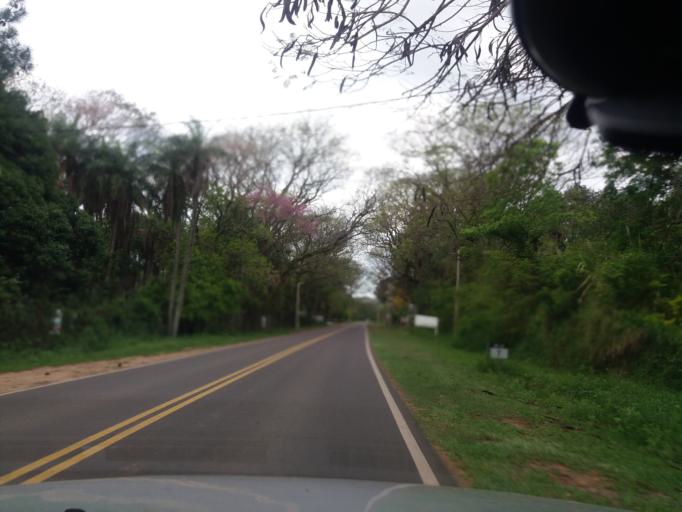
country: AR
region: Corrientes
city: Riachuelo
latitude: -27.4568
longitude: -58.6820
